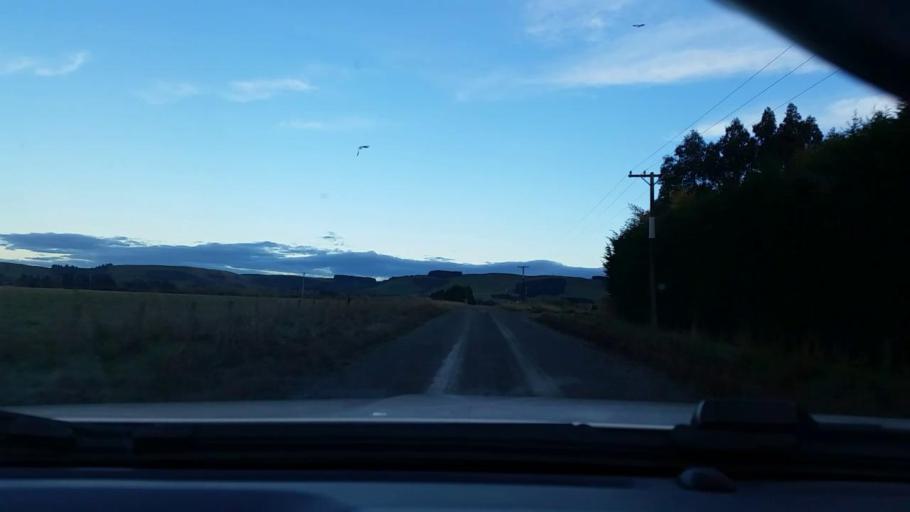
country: NZ
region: Southland
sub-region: Southland District
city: Winton
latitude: -46.1091
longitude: 168.4397
